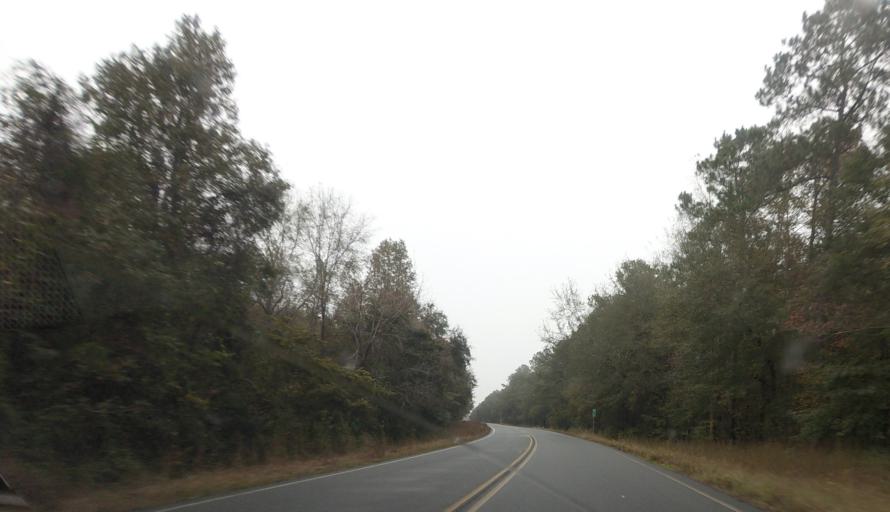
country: US
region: Georgia
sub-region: Marion County
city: Buena Vista
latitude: 32.3438
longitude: -84.4849
